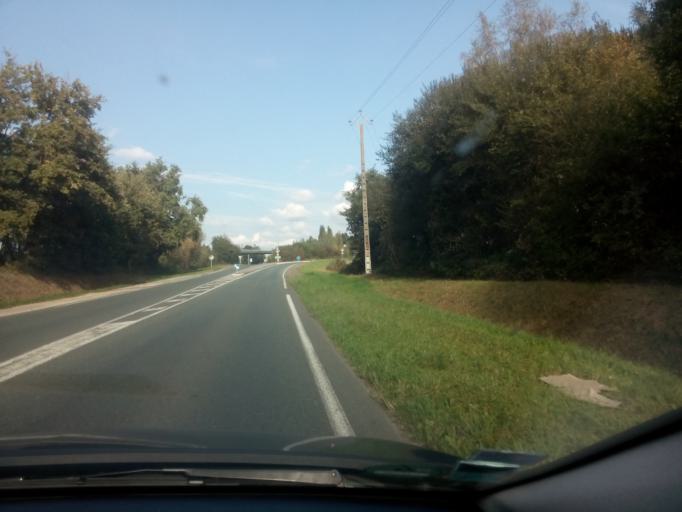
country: FR
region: Pays de la Loire
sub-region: Departement de Maine-et-Loire
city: Ecouflant
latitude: 47.5223
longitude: -0.5025
